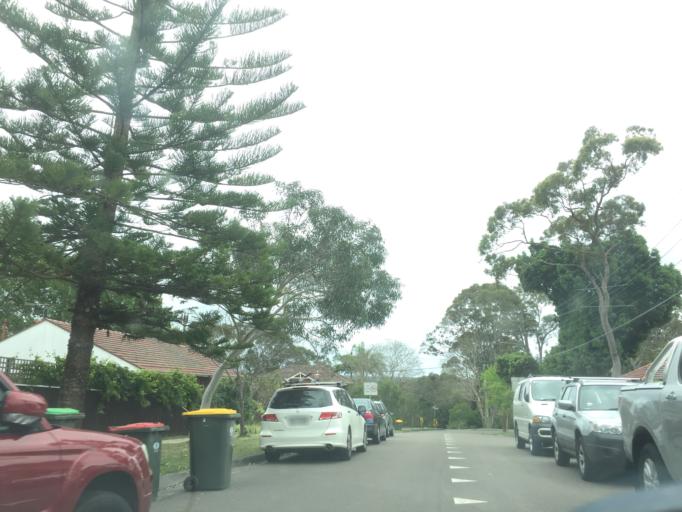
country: AU
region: New South Wales
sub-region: Willoughby
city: Lane Cove North
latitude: -33.8036
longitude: 151.1575
